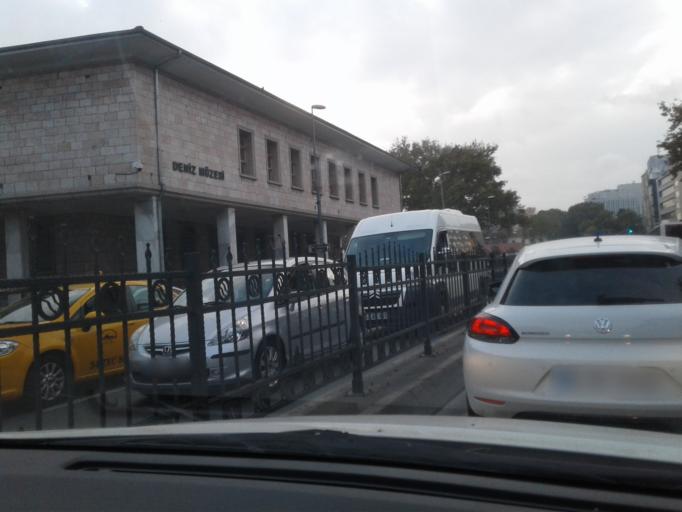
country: TR
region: Istanbul
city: UEskuedar
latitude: 41.0419
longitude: 29.0059
